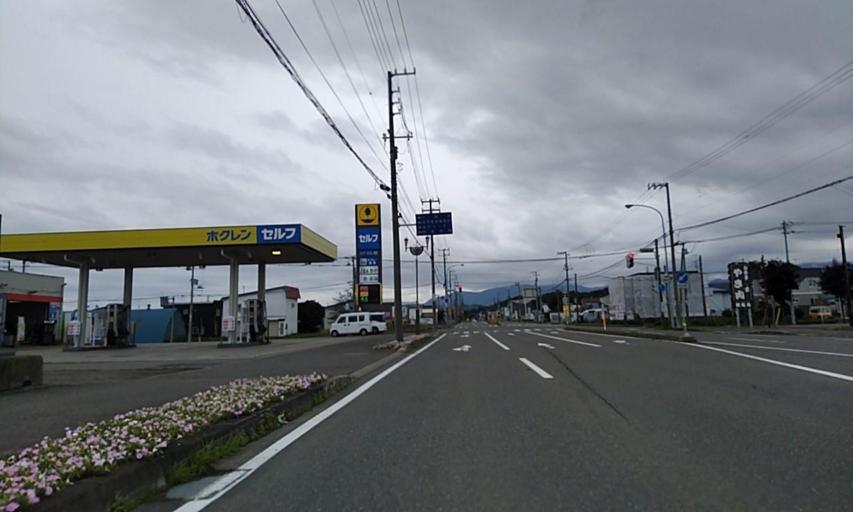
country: JP
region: Hokkaido
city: Obihiro
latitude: 42.3031
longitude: 143.3171
